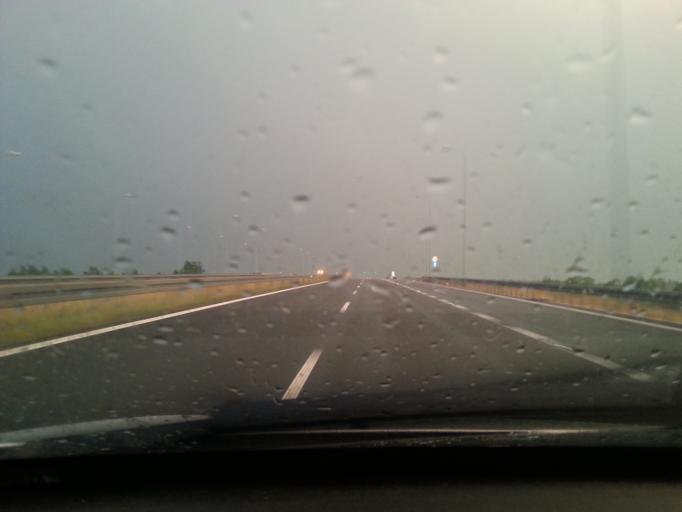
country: PL
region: Lodz Voivodeship
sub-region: Powiat pabianicki
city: Dobron
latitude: 51.6424
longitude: 19.2709
